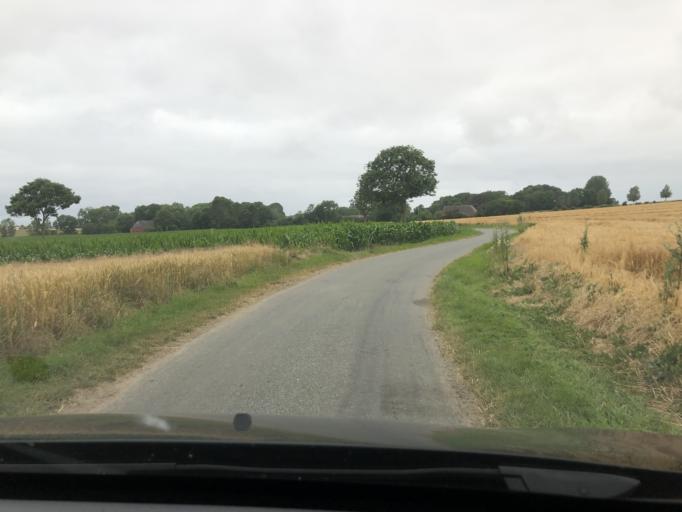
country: DK
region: South Denmark
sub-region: AEro Kommune
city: AEroskobing
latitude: 54.8402
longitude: 10.4243
